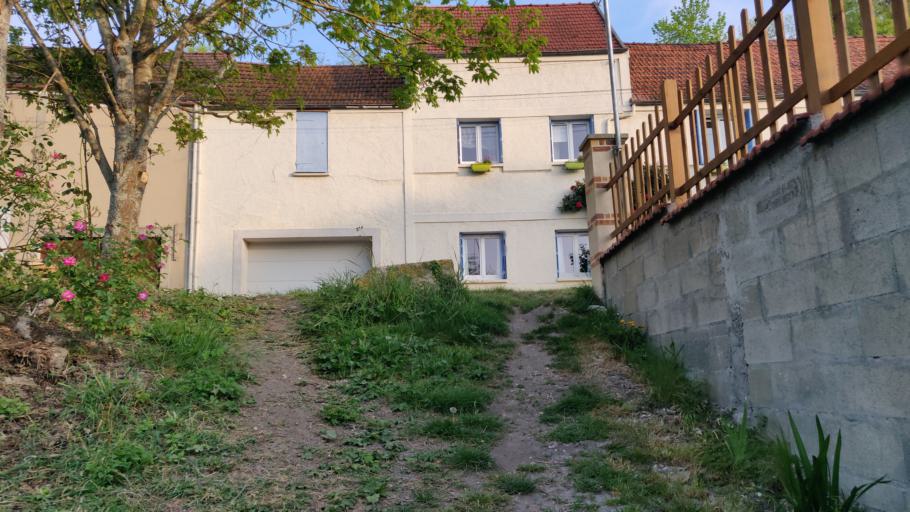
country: FR
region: Ile-de-France
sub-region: Departement des Yvelines
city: Freneuse
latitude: 49.0386
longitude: 1.6333
